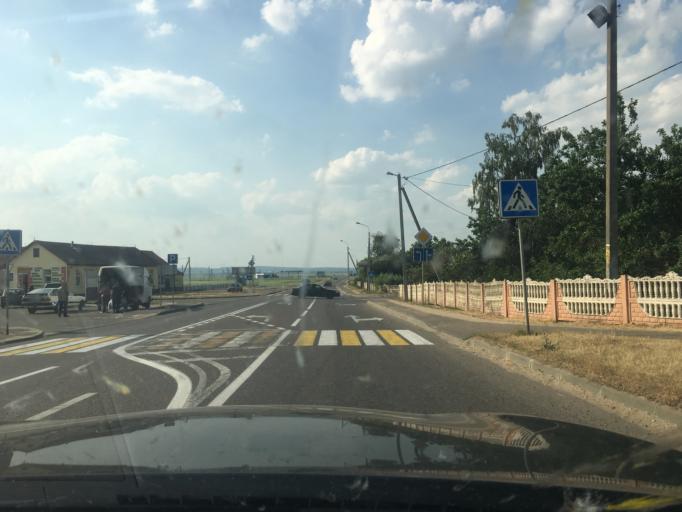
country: BY
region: Grodnenskaya
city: Indura
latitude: 53.3411
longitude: 23.9487
